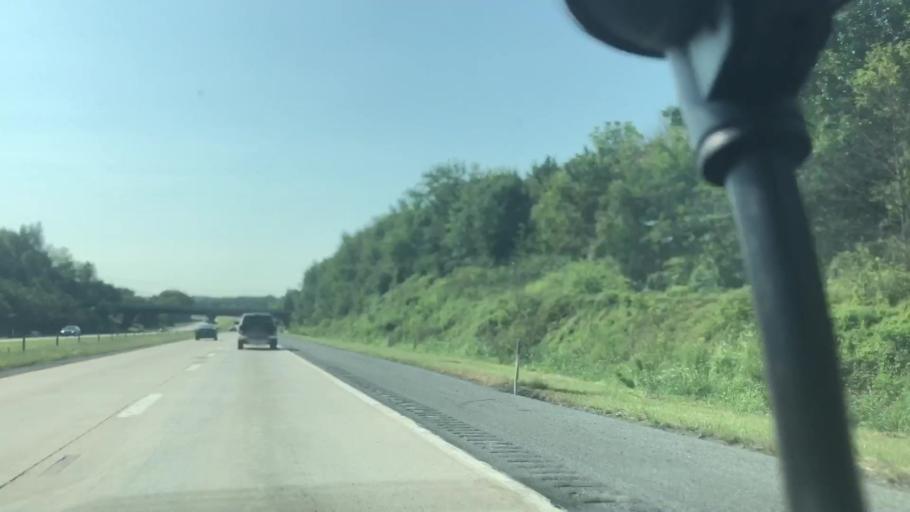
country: US
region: Pennsylvania
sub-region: Montgomery County
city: Royersford
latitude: 40.2058
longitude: -75.5370
